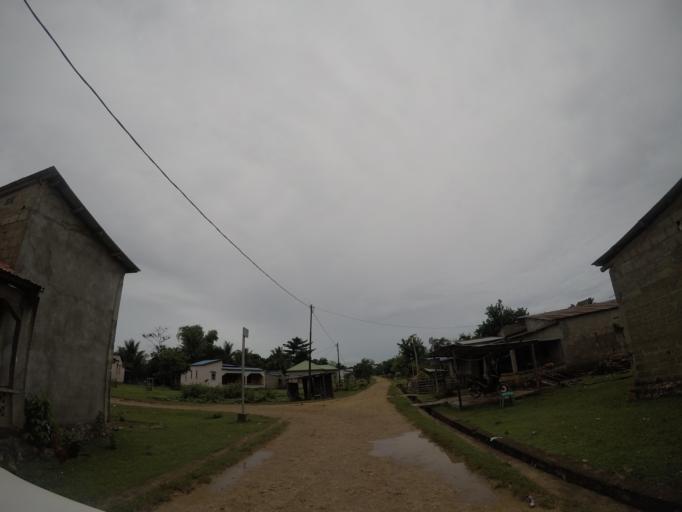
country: TL
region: Lautem
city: Lospalos
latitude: -8.5236
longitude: 127.0073
